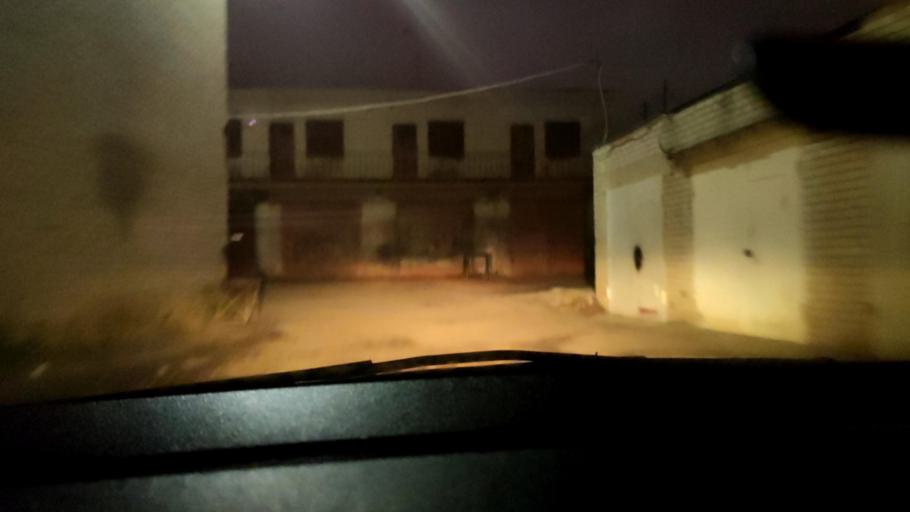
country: RU
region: Voronezj
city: Voronezh
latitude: 51.6775
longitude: 39.1796
